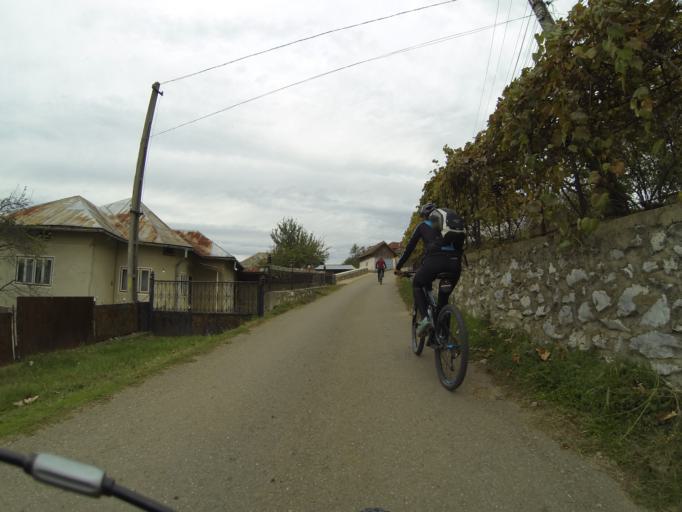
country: RO
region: Gorj
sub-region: Comuna Tismana
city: Sohodol
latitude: 45.0503
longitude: 22.8969
